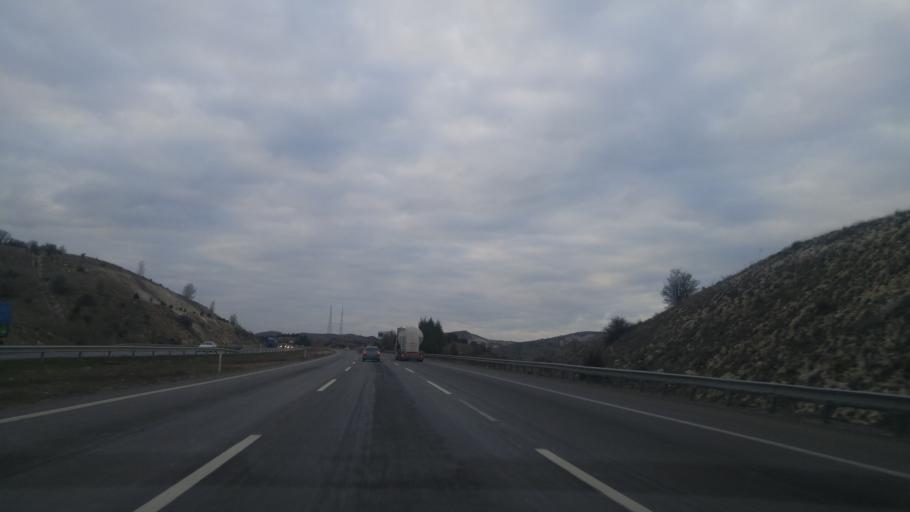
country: TR
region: Ankara
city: Kazan
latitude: 40.2120
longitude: 32.5660
